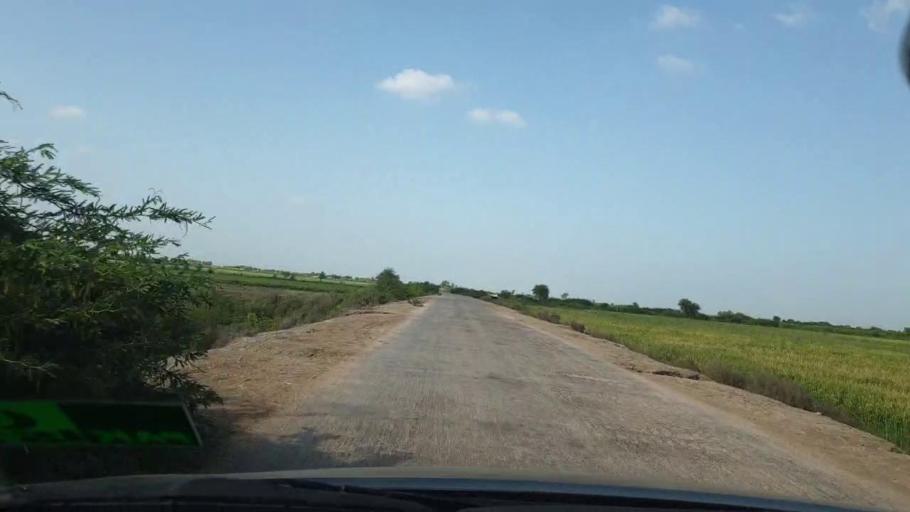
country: PK
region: Sindh
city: Tando Bago
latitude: 24.7010
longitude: 69.1909
